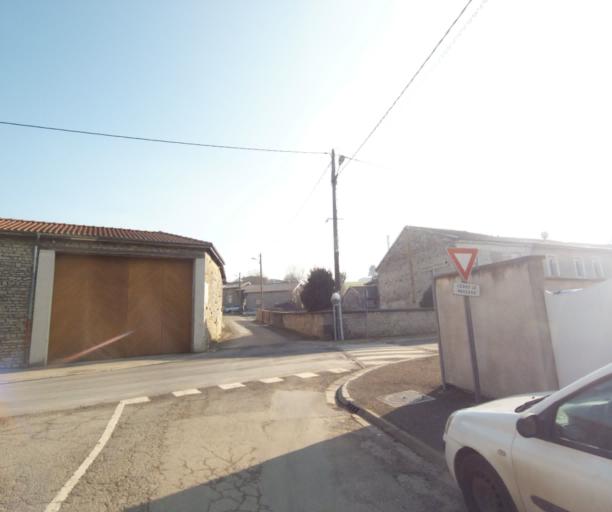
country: FR
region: Champagne-Ardenne
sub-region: Departement de la Haute-Marne
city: Wassy
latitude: 48.4708
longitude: 4.9710
